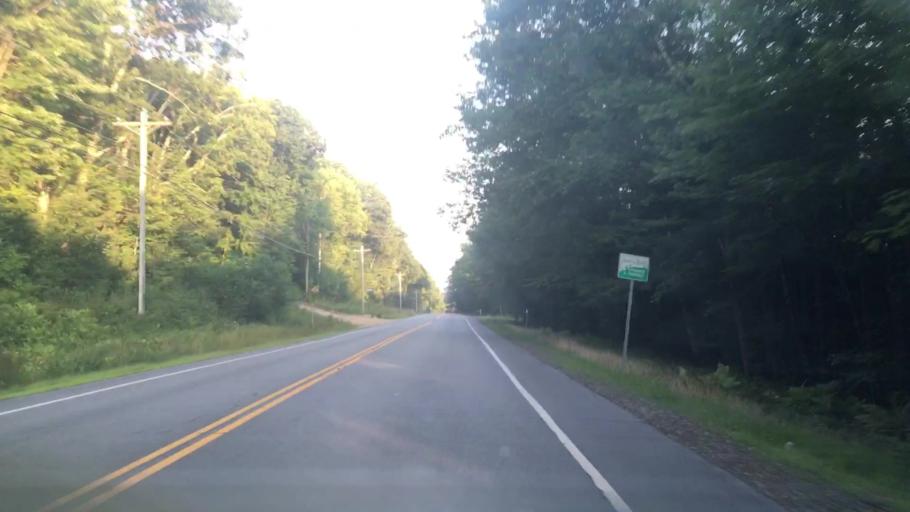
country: US
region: New Hampshire
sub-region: Belknap County
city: Gilmanton
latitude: 43.4292
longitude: -71.3768
